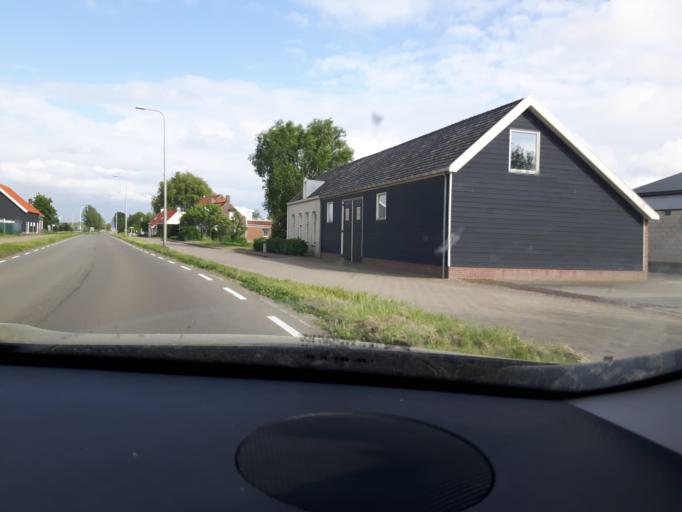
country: NL
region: Zeeland
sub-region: Gemeente Middelburg
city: Middelburg
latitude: 51.4593
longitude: 3.6113
